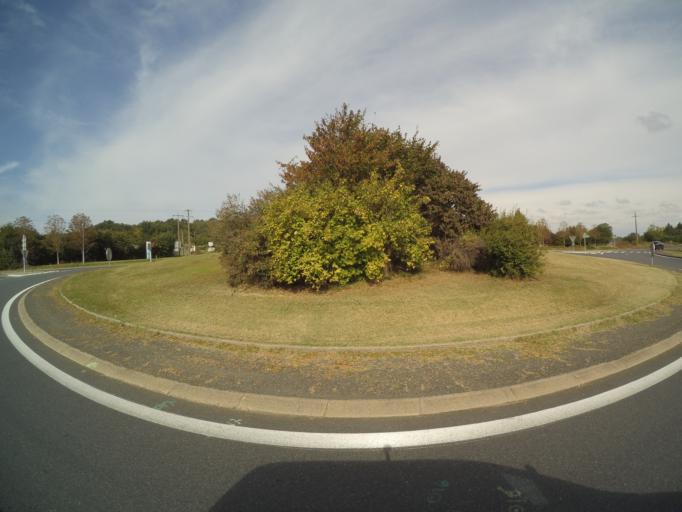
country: FR
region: Pays de la Loire
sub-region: Departement de Maine-et-Loire
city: Distre
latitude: 47.2309
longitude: -0.1243
